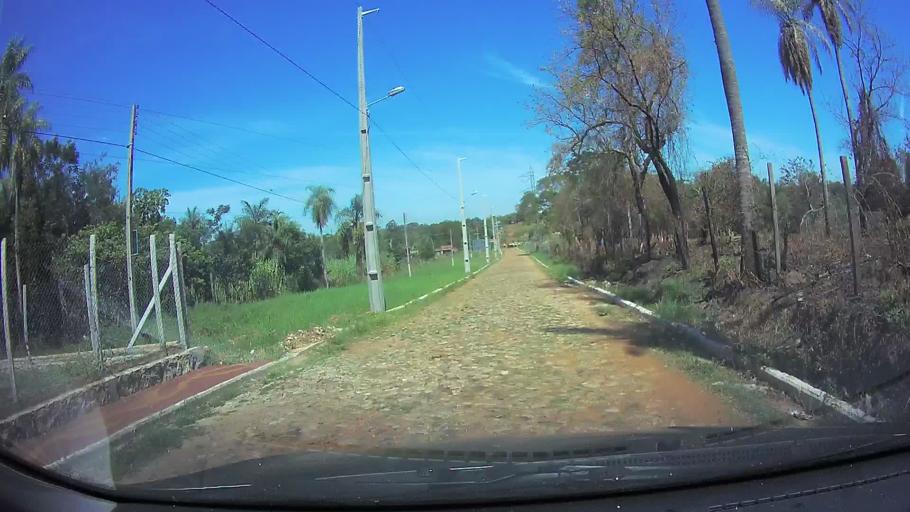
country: PY
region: Central
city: Limpio
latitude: -25.2347
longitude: -57.4384
